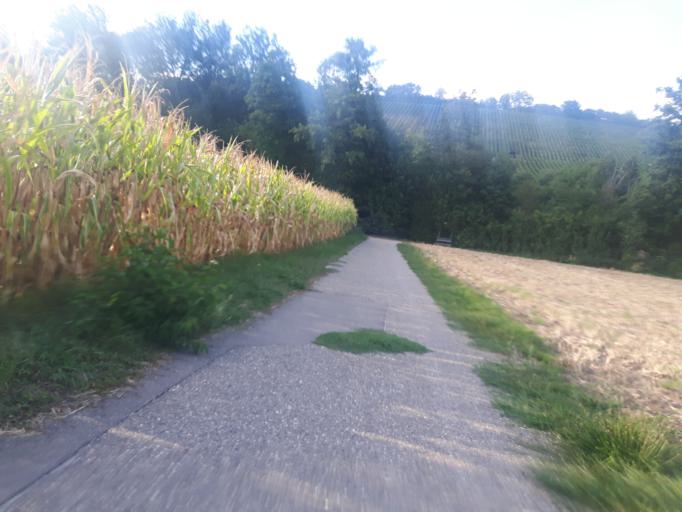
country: DE
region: Baden-Wuerttemberg
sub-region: Regierungsbezirk Stuttgart
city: Zaberfeld
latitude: 49.0580
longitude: 8.9455
